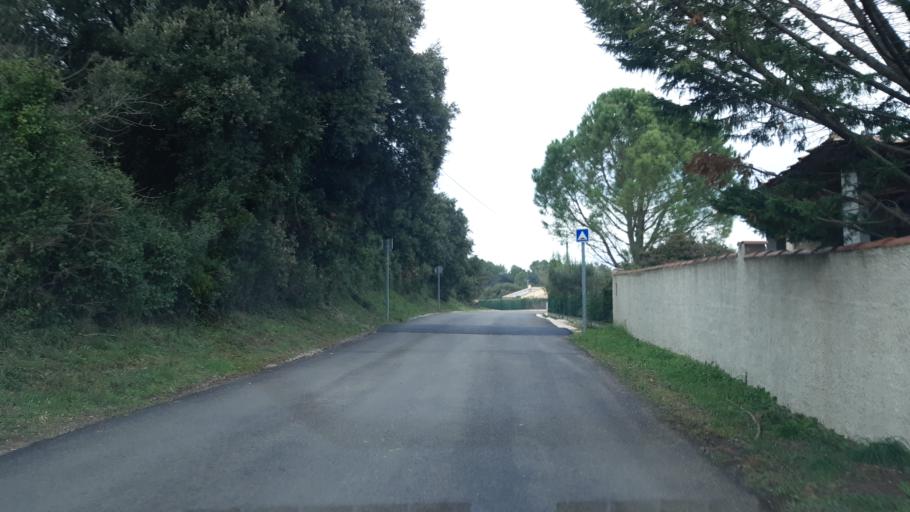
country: FR
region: Languedoc-Roussillon
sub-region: Departement du Gard
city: Comps
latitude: 43.8428
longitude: 4.6039
